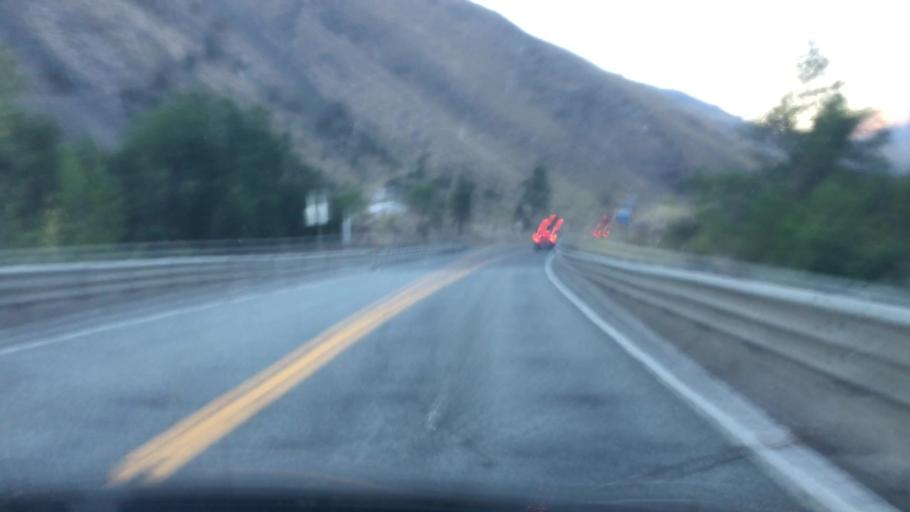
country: US
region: Idaho
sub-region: Valley County
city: McCall
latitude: 45.3575
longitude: -116.3610
